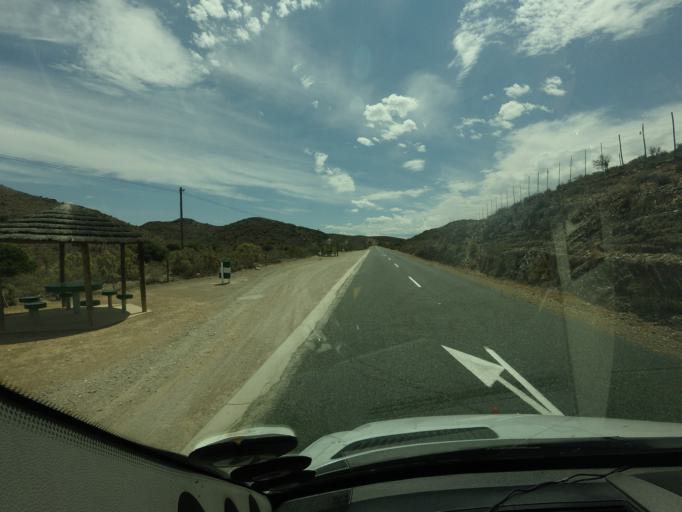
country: ZA
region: Western Cape
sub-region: Eden District Municipality
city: Ladismith
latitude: -33.7042
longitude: 20.9674
